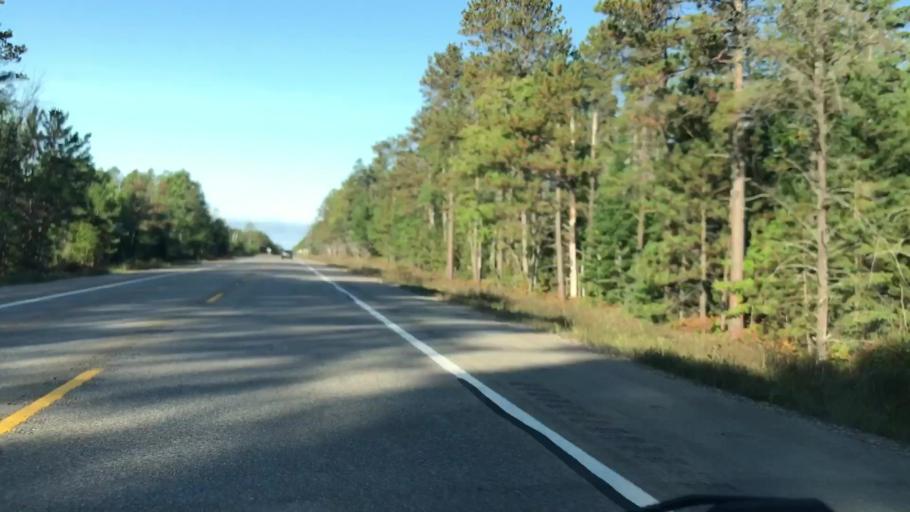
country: US
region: Michigan
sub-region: Chippewa County
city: Sault Ste. Marie
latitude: 46.3708
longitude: -84.7314
